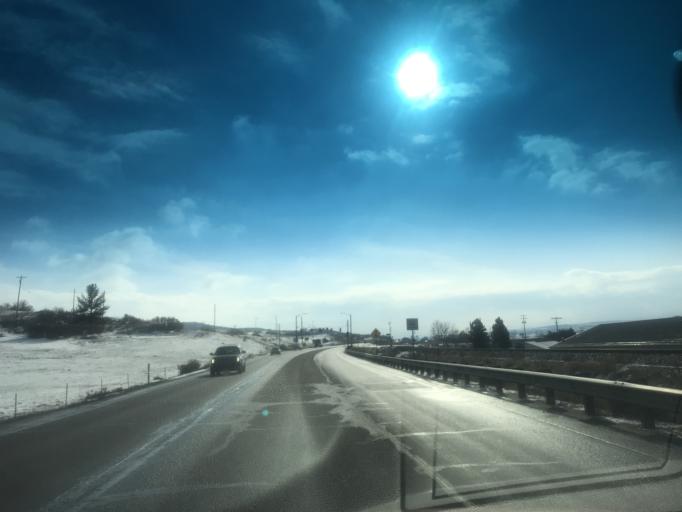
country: US
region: Colorado
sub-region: Douglas County
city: Highlands Ranch
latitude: 39.4728
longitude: -104.9895
